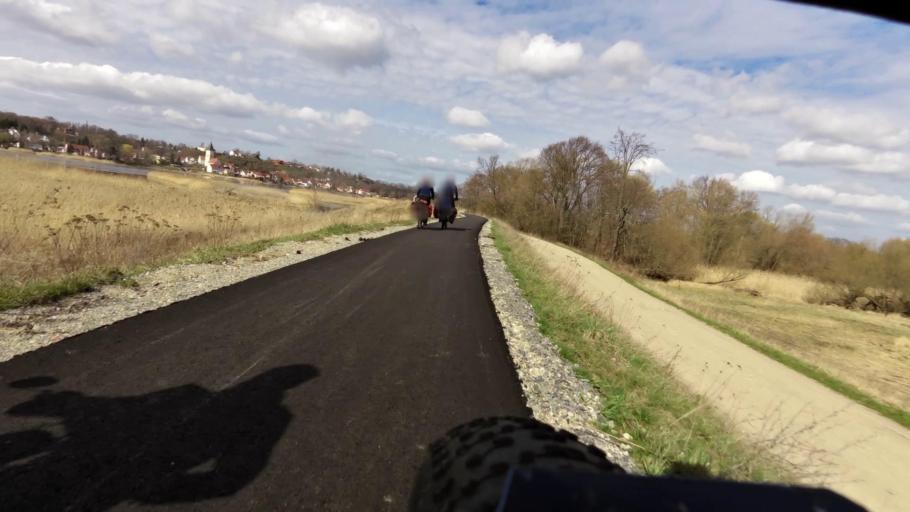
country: DE
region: Brandenburg
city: Lebus
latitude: 52.4204
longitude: 14.5477
